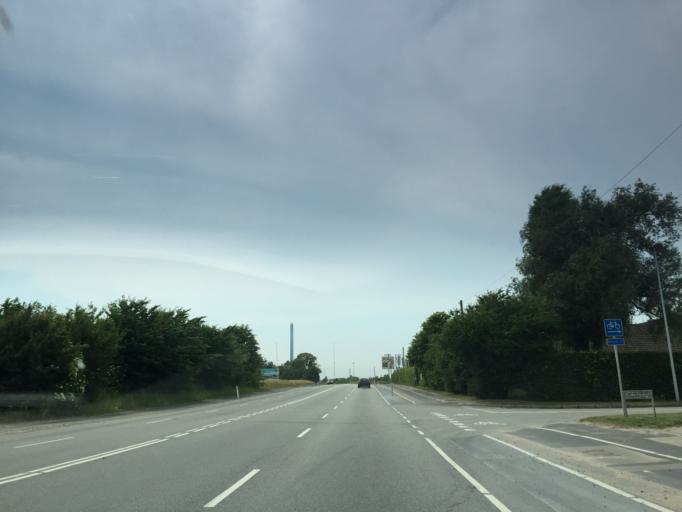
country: DK
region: Zealand
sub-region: Roskilde Kommune
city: Vindinge
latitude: 55.6445
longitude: 12.1392
